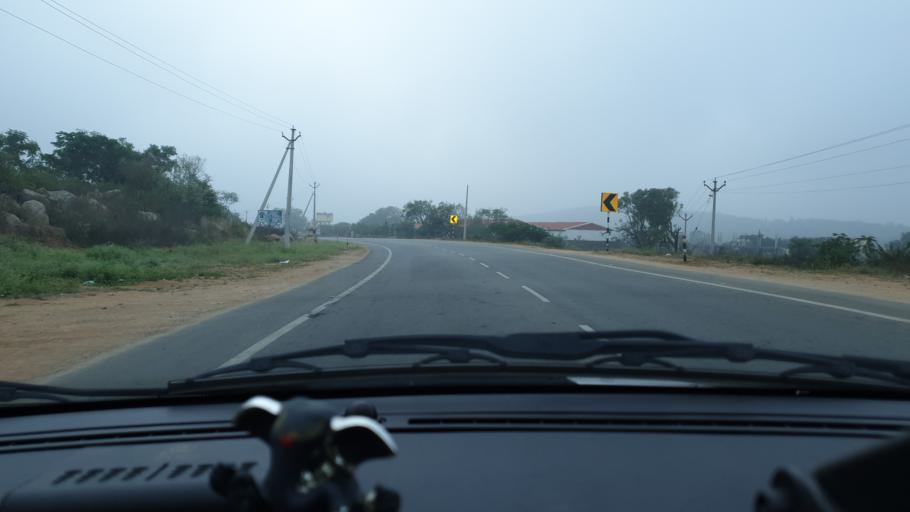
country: IN
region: Telangana
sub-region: Mahbubnagar
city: Farrukhnagar
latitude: 16.9574
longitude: 78.5137
